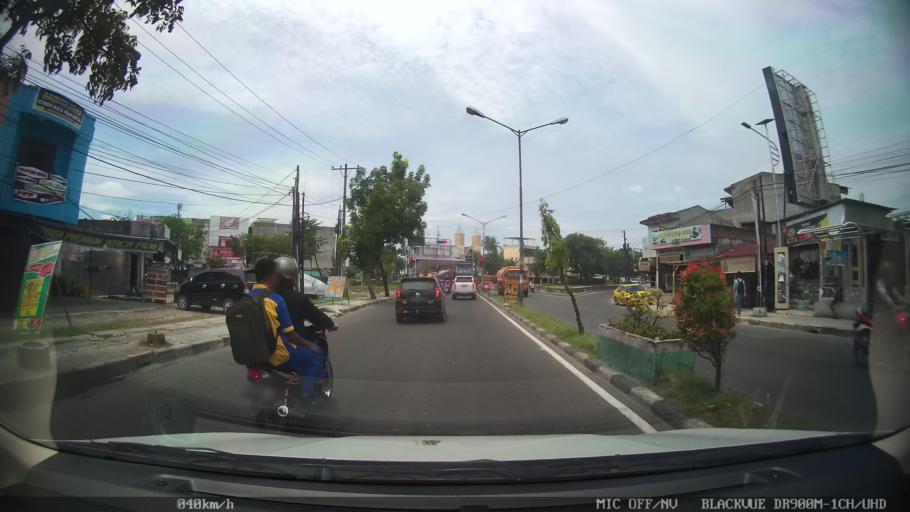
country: ID
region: North Sumatra
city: Sunggal
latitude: 3.5417
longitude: 98.6229
